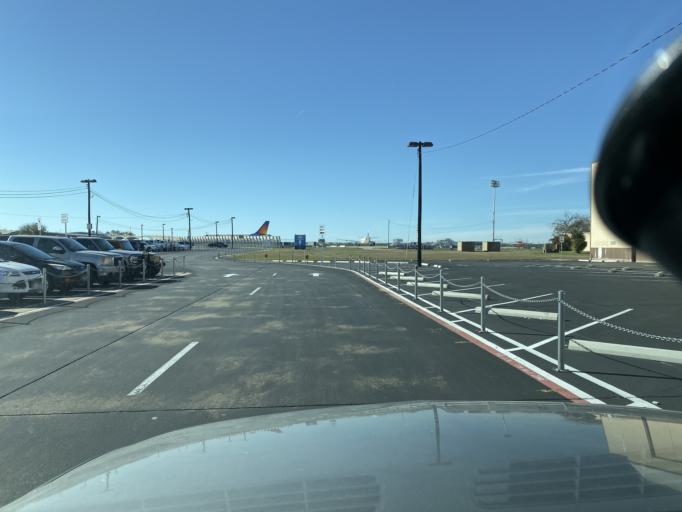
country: US
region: Texas
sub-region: Travis County
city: Hornsby Bend
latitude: 30.1945
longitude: -97.6679
